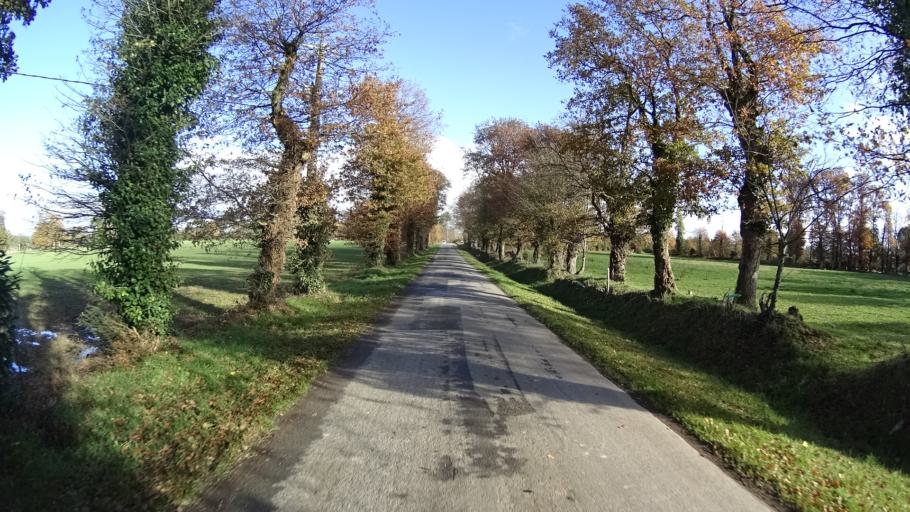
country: FR
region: Brittany
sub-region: Departement du Morbihan
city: Carentoir
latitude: 47.8293
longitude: -2.0931
